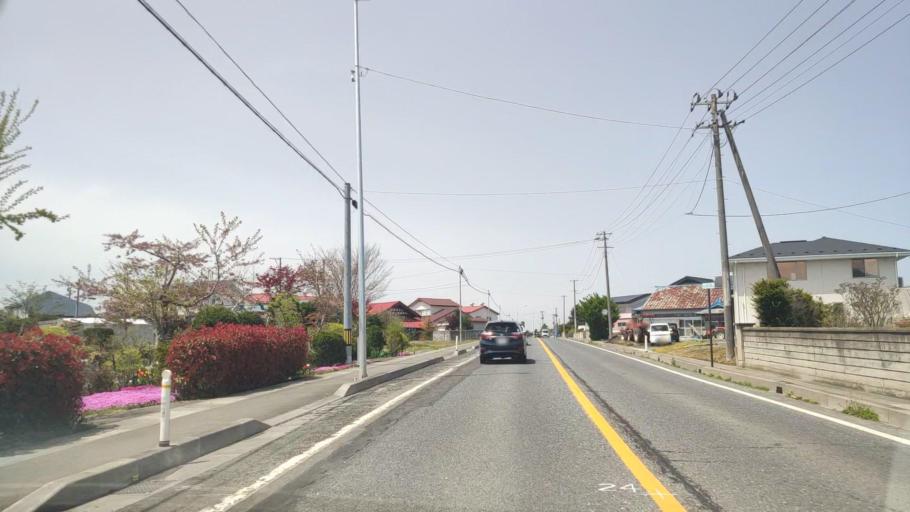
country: JP
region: Aomori
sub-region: Misawa Shi
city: Inuotose
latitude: 40.6079
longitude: 141.2862
